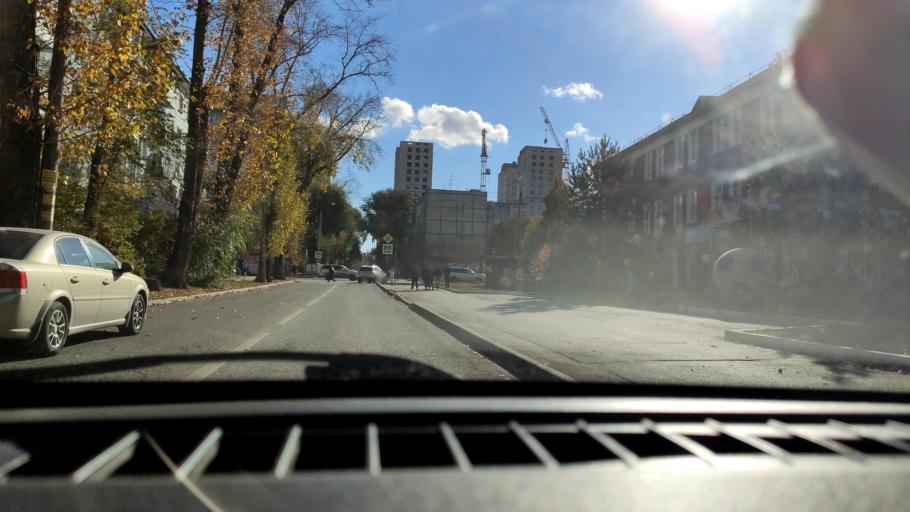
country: RU
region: Samara
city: Samara
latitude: 53.2131
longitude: 50.1580
